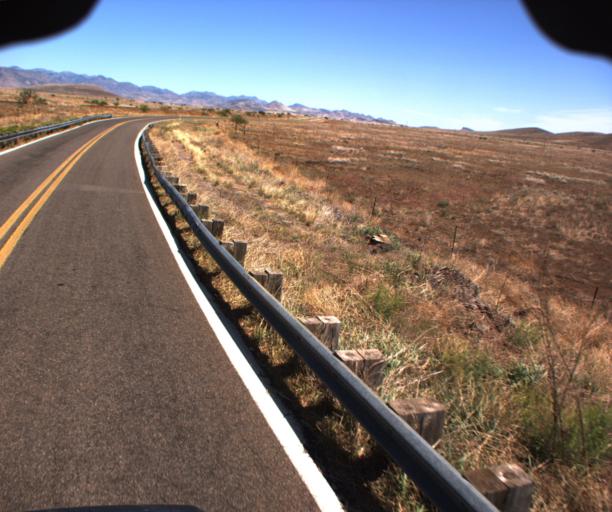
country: US
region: Arizona
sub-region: Cochise County
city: Douglas
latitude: 31.5621
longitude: -109.2654
